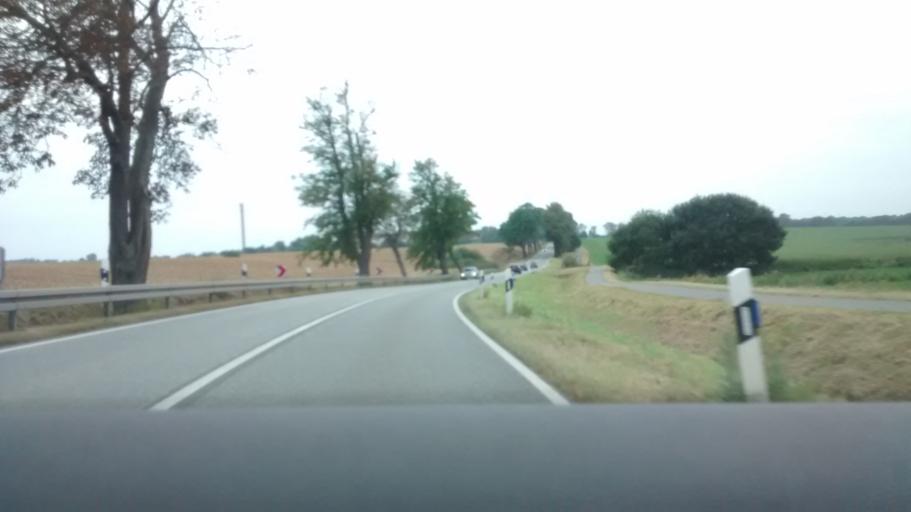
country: DE
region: Mecklenburg-Vorpommern
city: Mecklenburg
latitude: 53.8233
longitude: 11.4547
